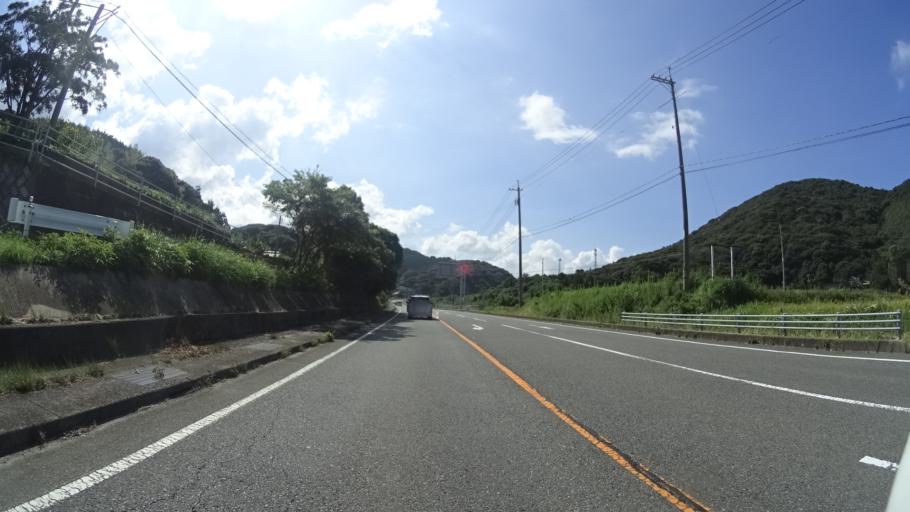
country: JP
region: Yamaguchi
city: Shimonoseki
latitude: 34.2247
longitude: 130.9300
